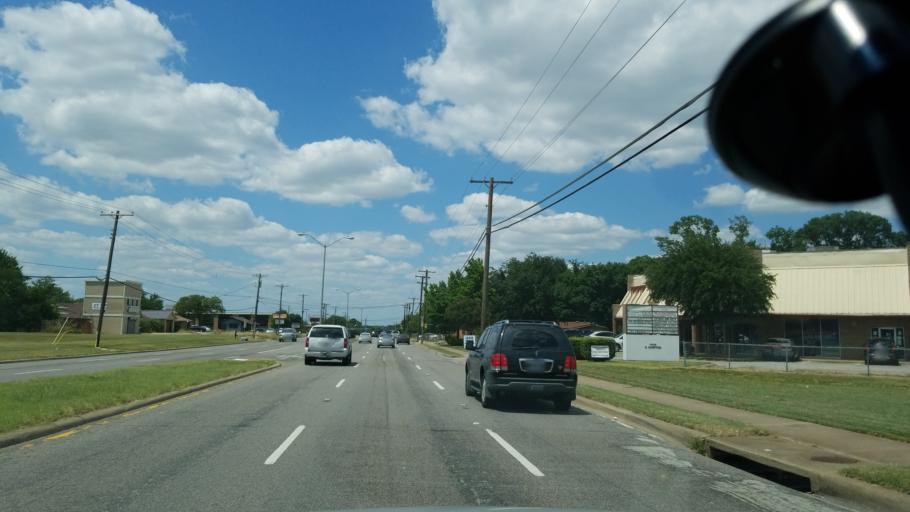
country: US
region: Texas
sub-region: Dallas County
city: Cockrell Hill
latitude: 32.6872
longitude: -96.8570
